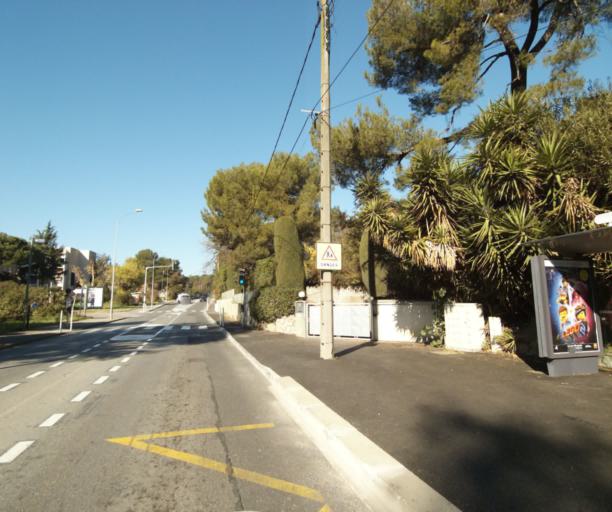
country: FR
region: Provence-Alpes-Cote d'Azur
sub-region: Departement des Alpes-Maritimes
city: Biot
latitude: 43.5991
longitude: 7.1012
